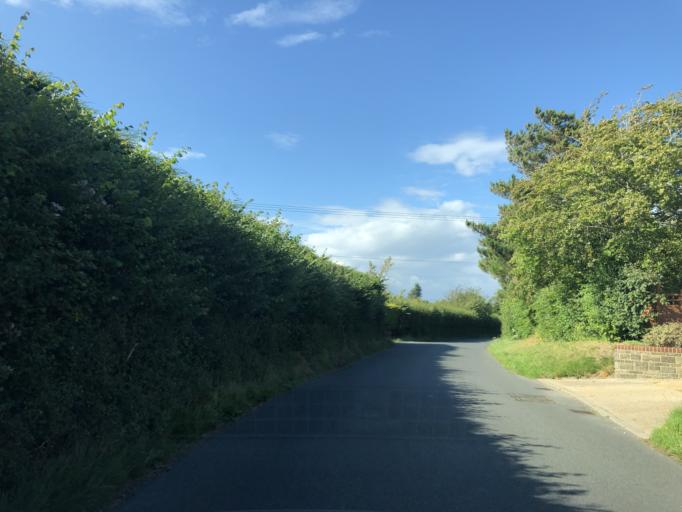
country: GB
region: England
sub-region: Isle of Wight
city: Shalfleet
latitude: 50.6843
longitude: -1.4003
